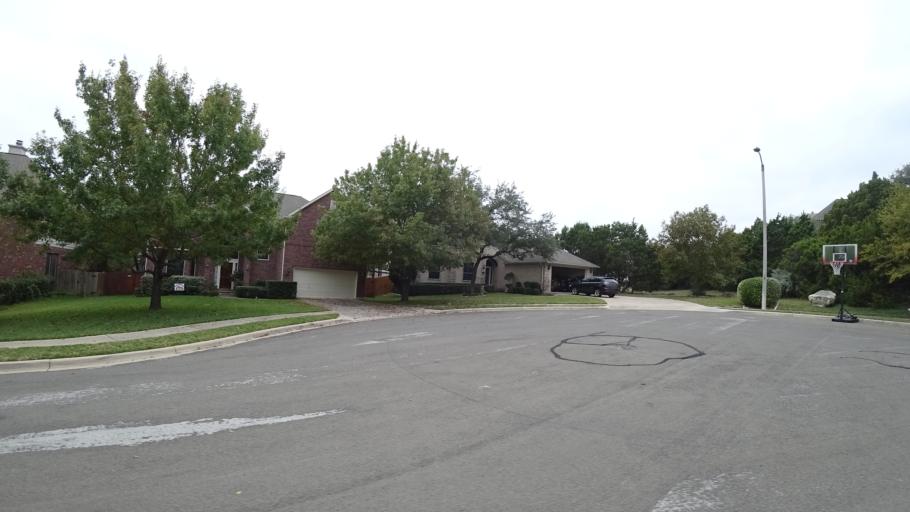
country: US
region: Texas
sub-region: Williamson County
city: Anderson Mill
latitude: 30.4340
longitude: -97.8188
